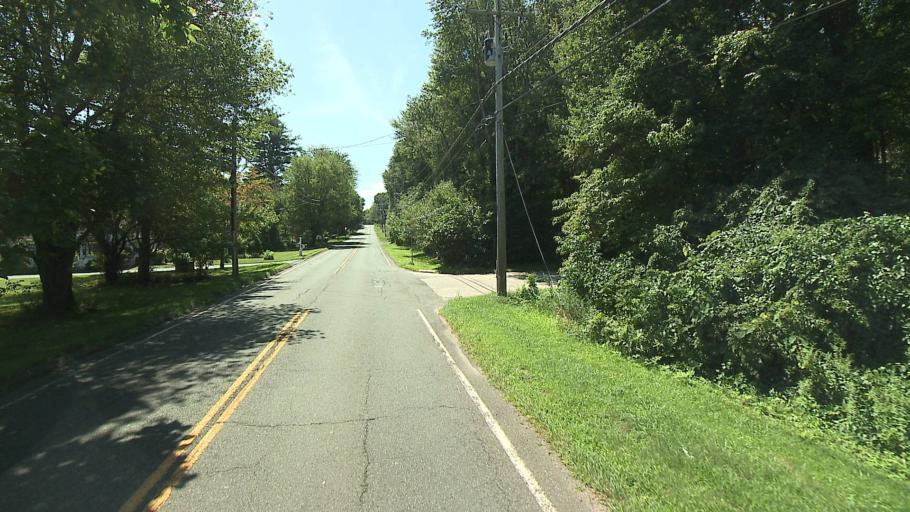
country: US
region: Connecticut
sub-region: Fairfield County
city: Trumbull
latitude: 41.3370
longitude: -73.2051
